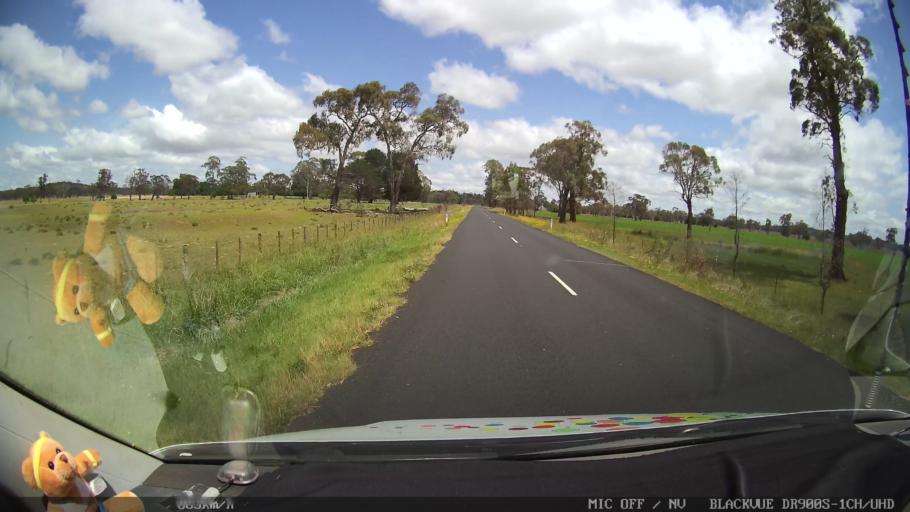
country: AU
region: New South Wales
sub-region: Glen Innes Severn
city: Glen Innes
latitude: -29.6320
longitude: 151.6776
